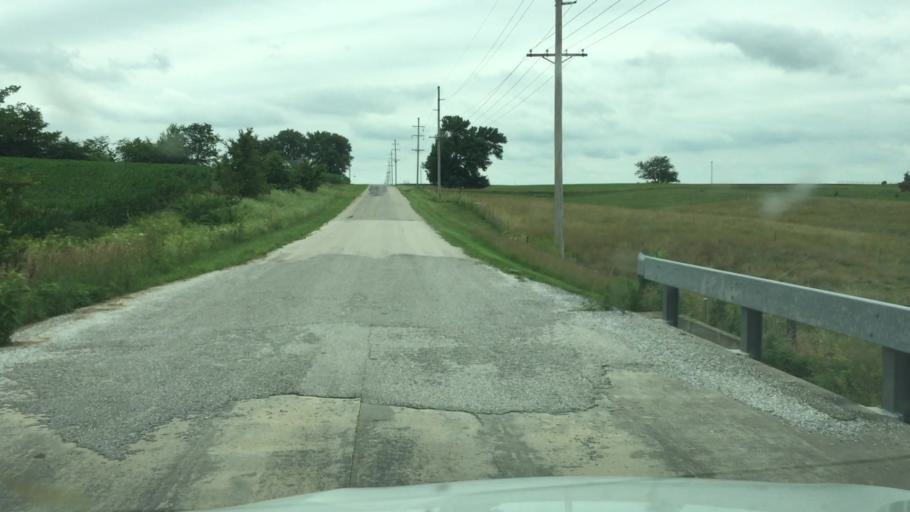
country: US
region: Illinois
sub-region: Hancock County
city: Carthage
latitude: 40.4036
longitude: -91.0824
